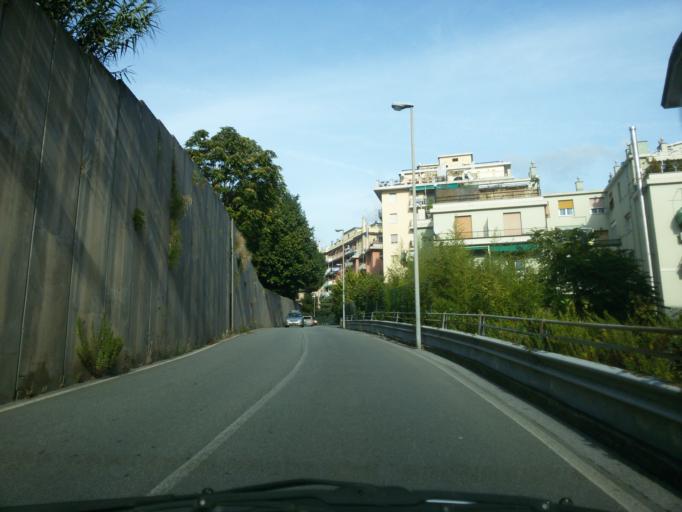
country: IT
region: Liguria
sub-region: Provincia di Genova
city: Piccarello
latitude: 44.4519
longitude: 8.9743
